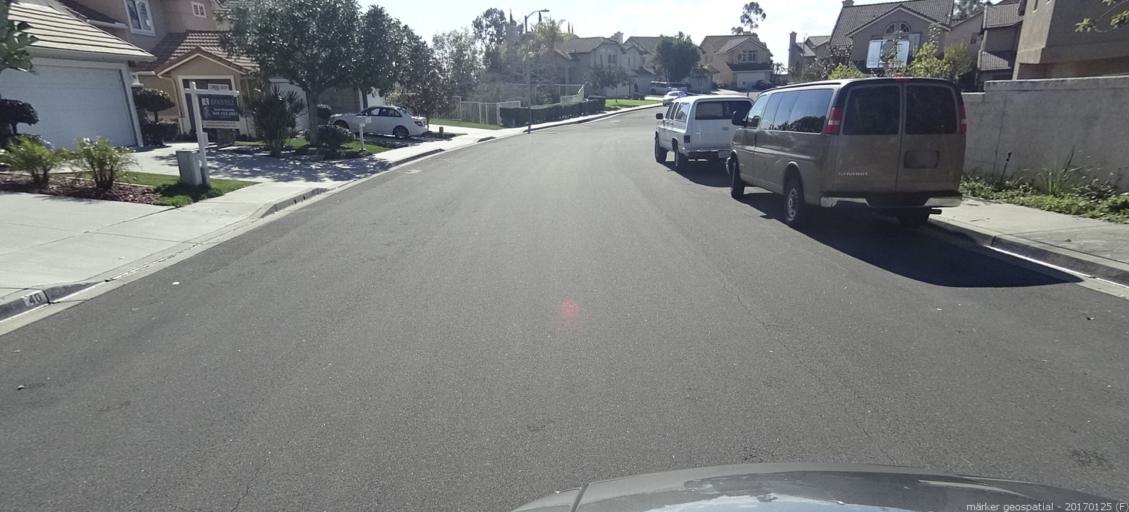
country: US
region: California
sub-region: Orange County
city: Foothill Ranch
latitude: 33.6852
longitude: -117.6491
